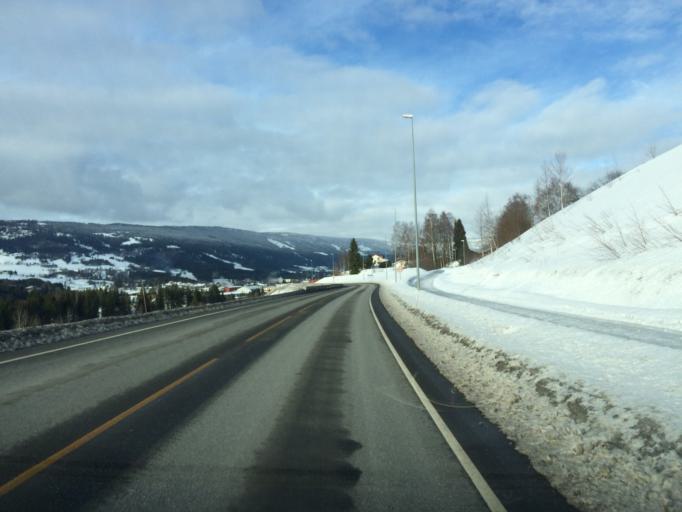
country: NO
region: Oppland
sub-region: Gausdal
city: Segalstad bru
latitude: 61.2218
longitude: 10.2402
